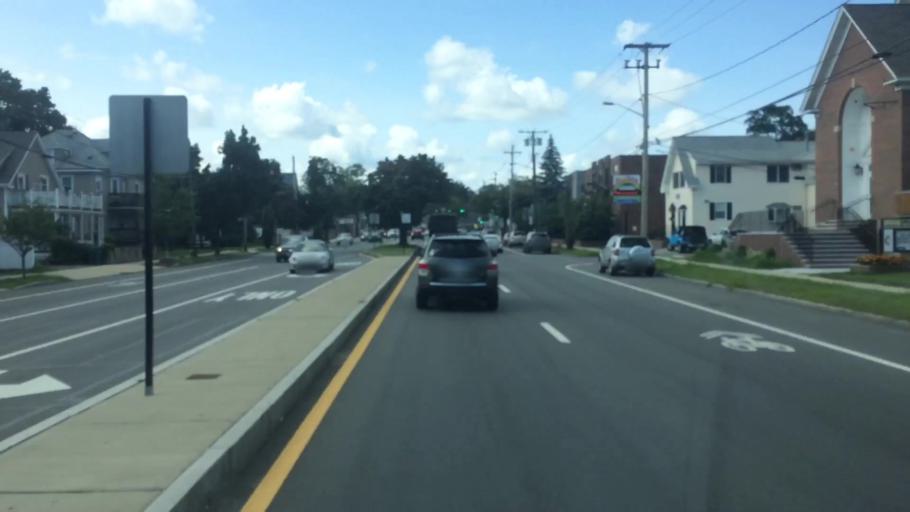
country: US
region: Massachusetts
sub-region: Essex County
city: Lynn
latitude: 42.4838
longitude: -70.9584
